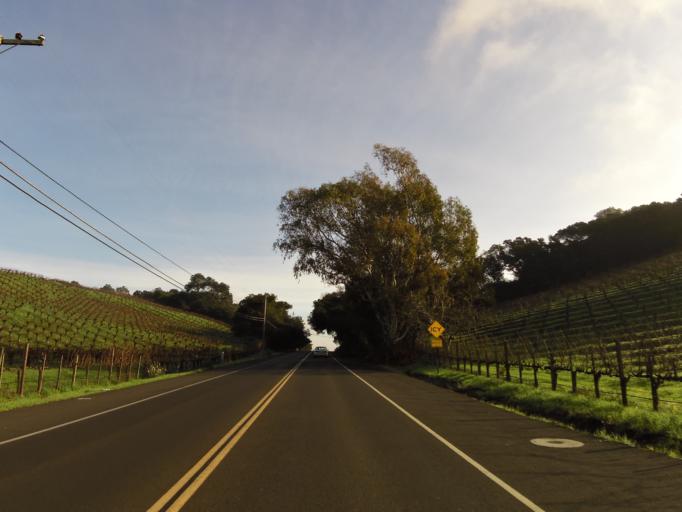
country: US
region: California
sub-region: Napa County
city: Napa
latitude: 38.2860
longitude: -122.3200
